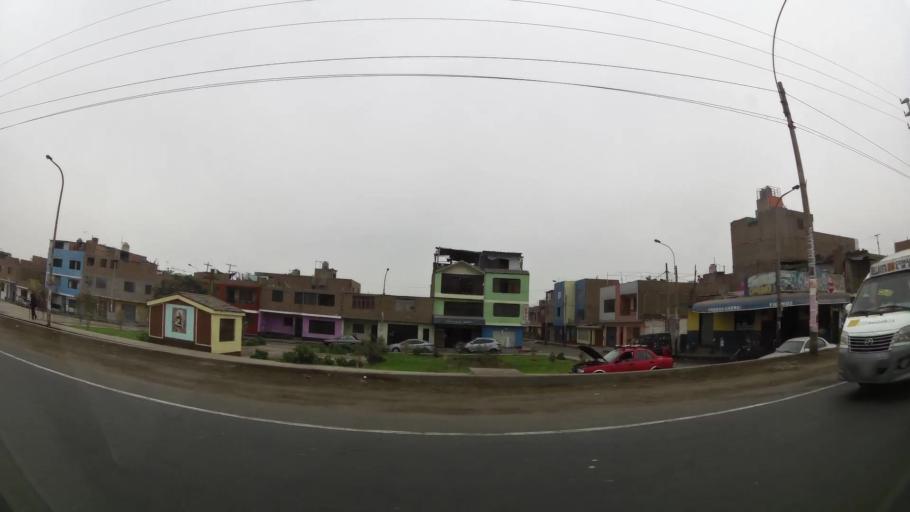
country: PE
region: Lima
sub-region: Lima
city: Urb. Santo Domingo
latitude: -11.9217
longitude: -77.0421
